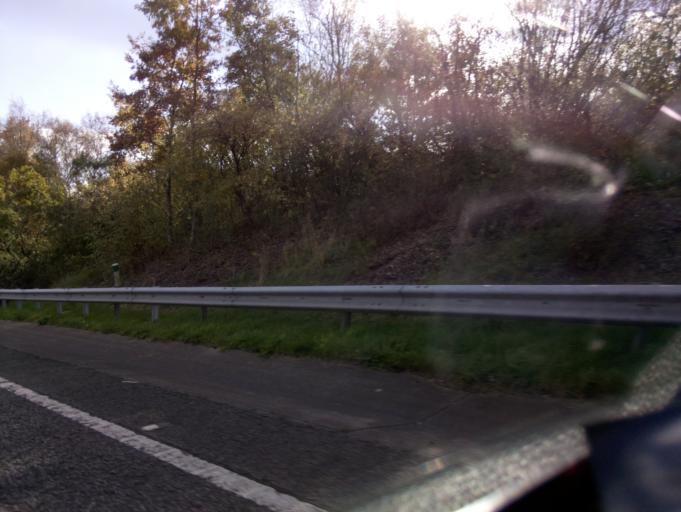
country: GB
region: Wales
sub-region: Merthyr Tydfil County Borough
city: Merthyr Tydfil
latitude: 51.7436
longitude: -3.3892
